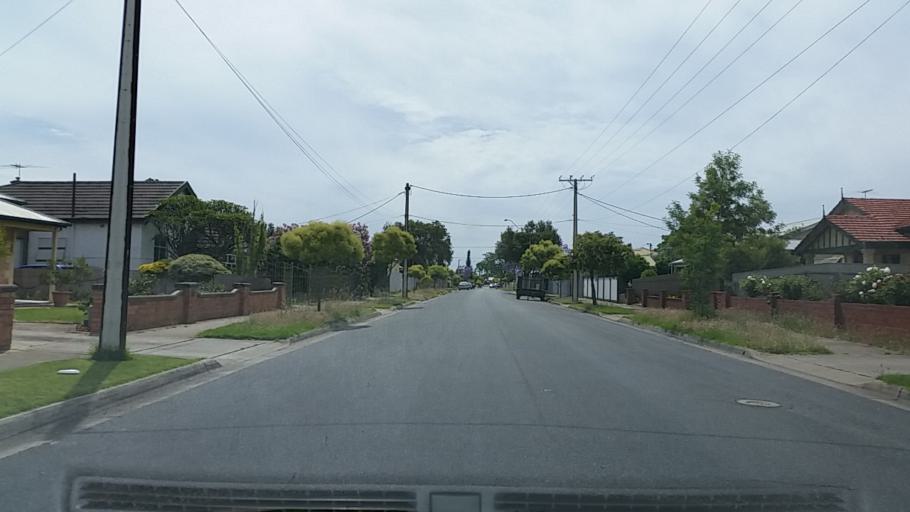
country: AU
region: South Australia
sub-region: Charles Sturt
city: Woodville
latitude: -34.8840
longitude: 138.5581
